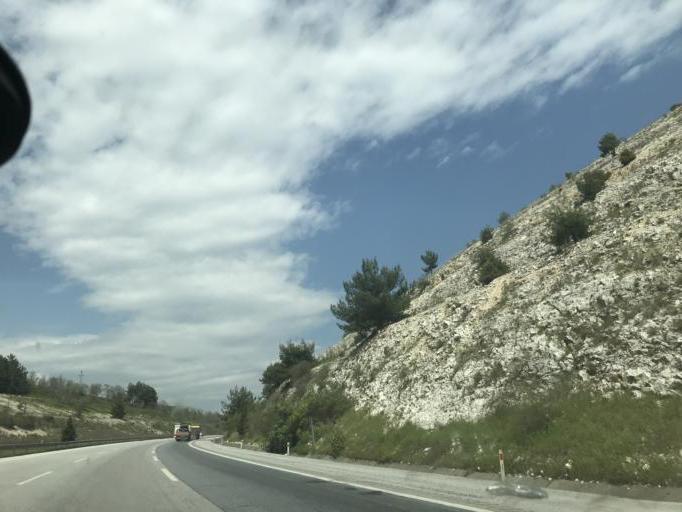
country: TR
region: Adana
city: Karaisali
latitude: 37.1576
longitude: 34.8409
